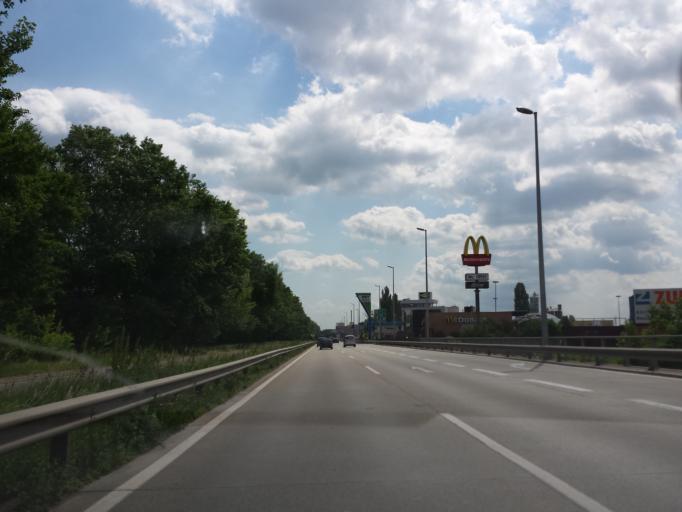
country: AT
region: Lower Austria
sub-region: Politischer Bezirk Wien-Umgebung
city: Schwechat
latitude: 48.1825
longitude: 16.4430
